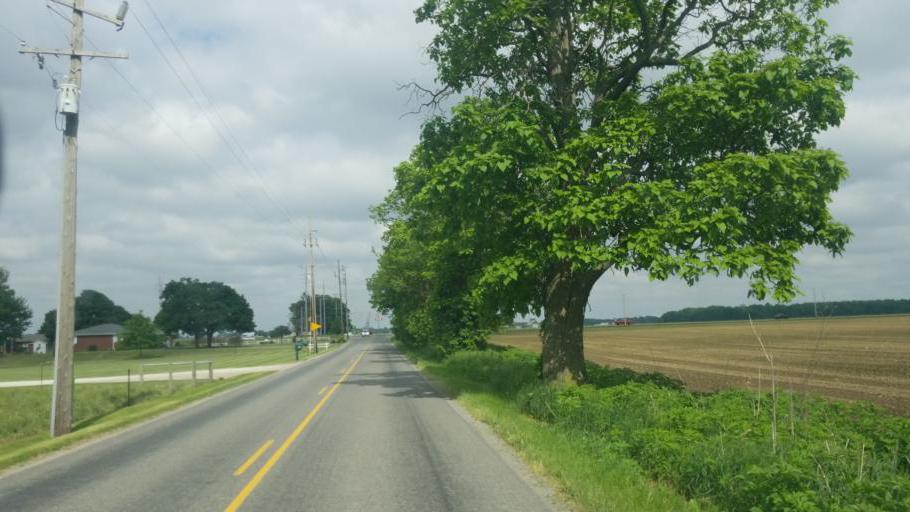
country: US
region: Indiana
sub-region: Elkhart County
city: Wakarusa
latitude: 41.4933
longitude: -86.0047
